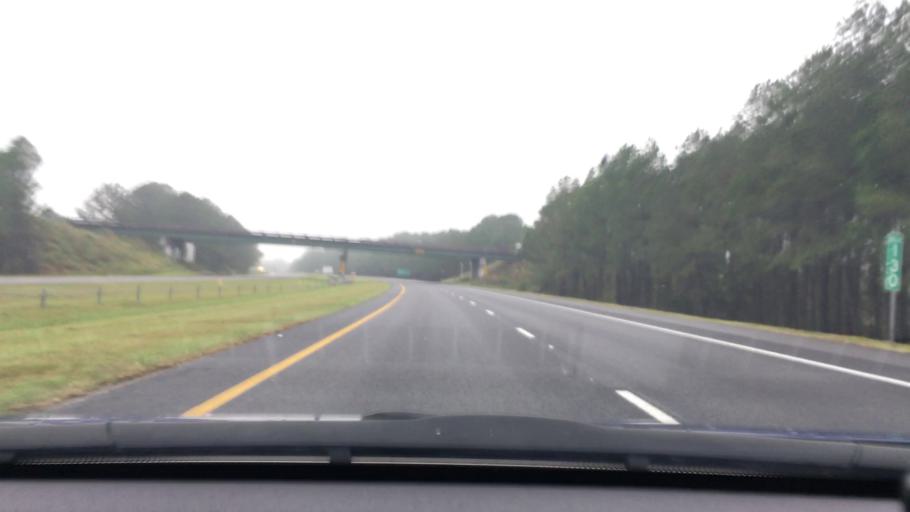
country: US
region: South Carolina
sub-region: Florence County
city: Timmonsville
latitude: 34.2083
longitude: -80.0397
